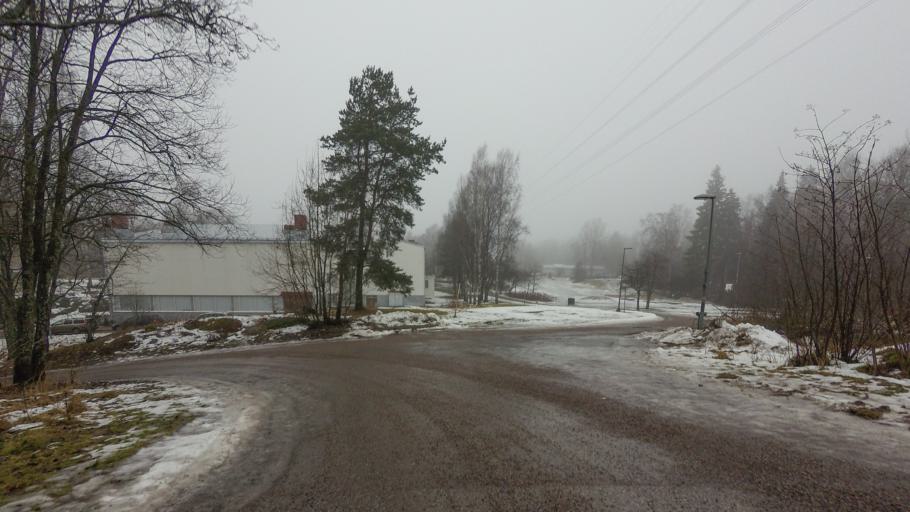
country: FI
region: Uusimaa
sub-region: Helsinki
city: Vantaa
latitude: 60.2089
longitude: 25.0450
